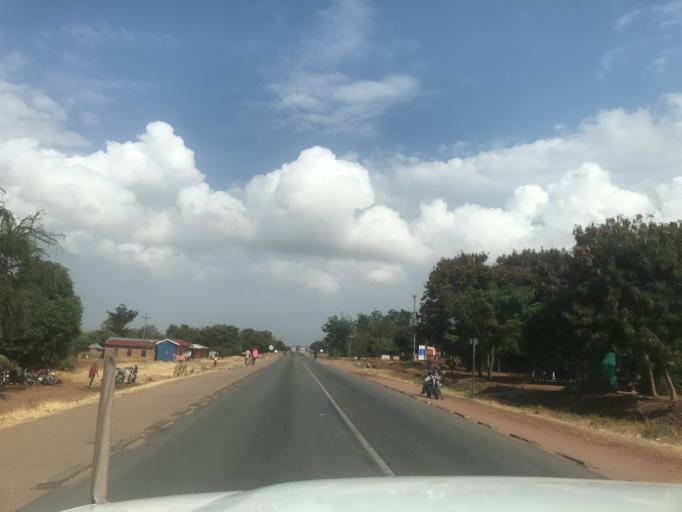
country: TZ
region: Mwanza
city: Usagara
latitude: -2.5554
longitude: 33.0384
